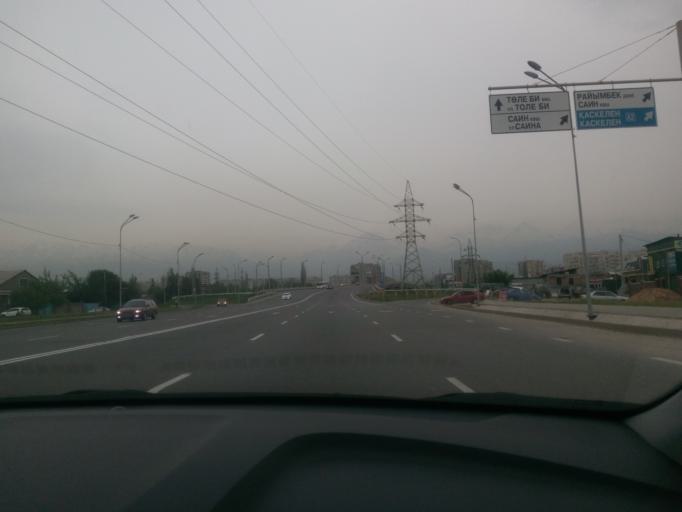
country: KZ
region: Almaty Qalasy
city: Almaty
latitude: 43.2473
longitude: 76.8259
